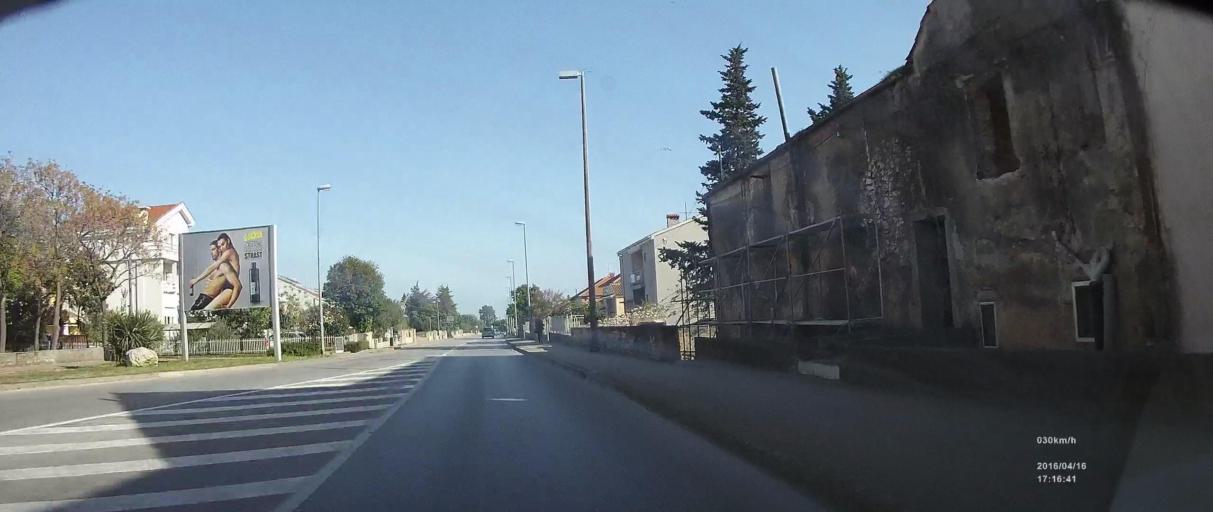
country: HR
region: Zadarska
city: Zadar
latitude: 44.1065
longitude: 15.2431
